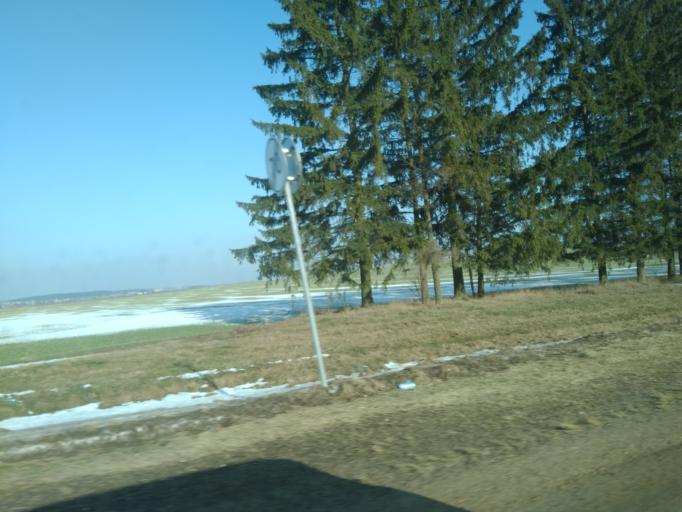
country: BY
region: Minsk
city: Snow
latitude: 53.2124
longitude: 26.4588
